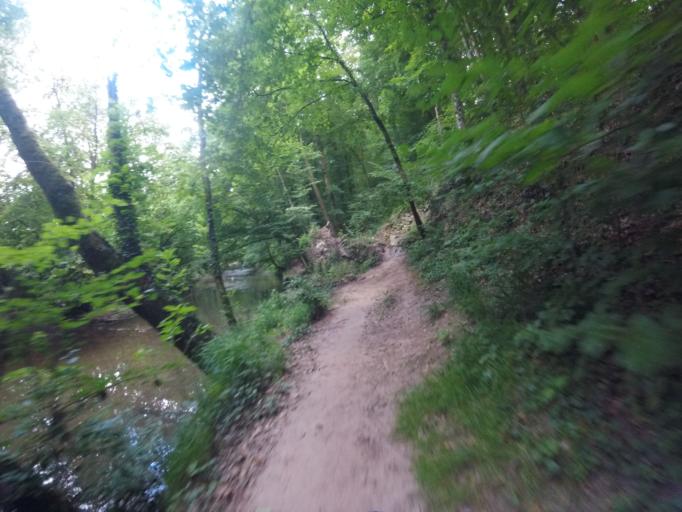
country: DE
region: Baden-Wuerttemberg
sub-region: Regierungsbezirk Stuttgart
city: Oppenweiler
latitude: 48.9605
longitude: 9.4618
